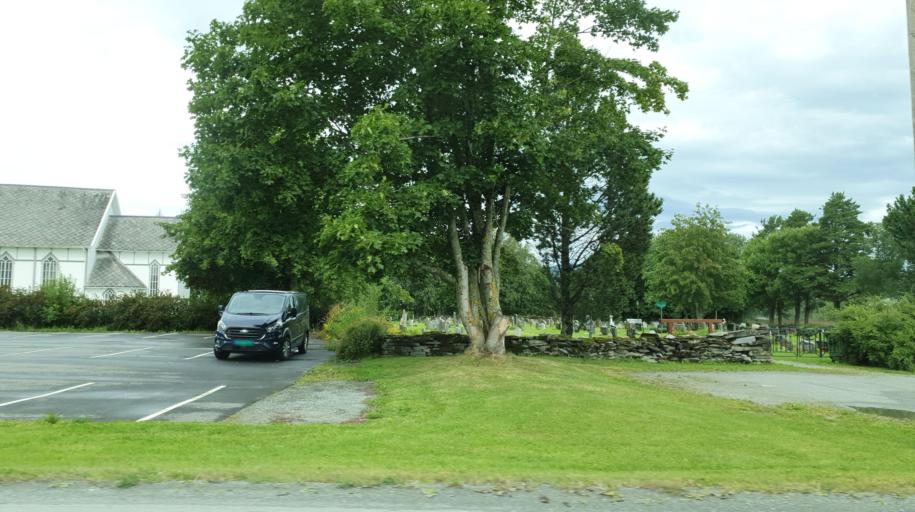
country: NO
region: Nord-Trondelag
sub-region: Stjordal
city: Stjordalshalsen
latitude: 63.4442
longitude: 10.9349
